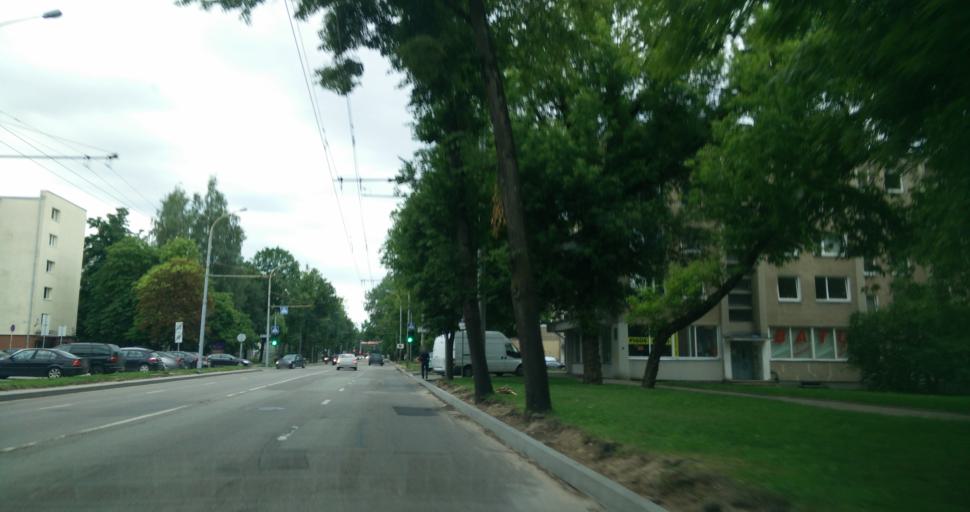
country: LT
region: Vilnius County
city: Rasos
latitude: 54.7146
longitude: 25.3157
